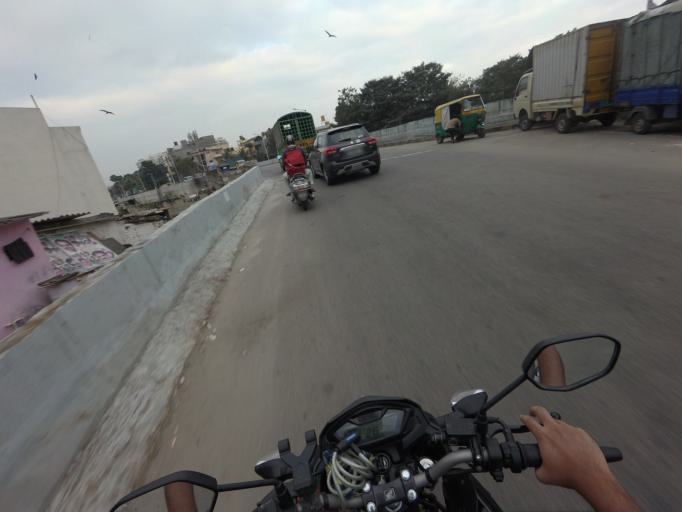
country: IN
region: Karnataka
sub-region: Bangalore Urban
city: Bangalore
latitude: 12.9663
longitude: 77.5451
